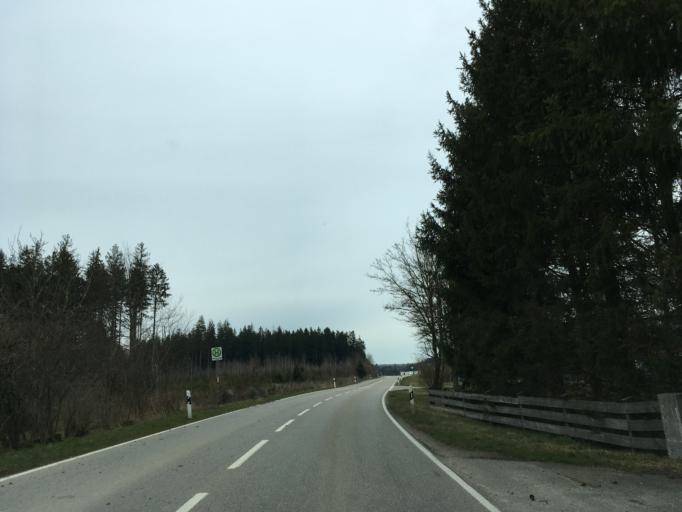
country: DE
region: Bavaria
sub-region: Upper Bavaria
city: Schnaitsee
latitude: 48.0805
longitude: 12.4105
